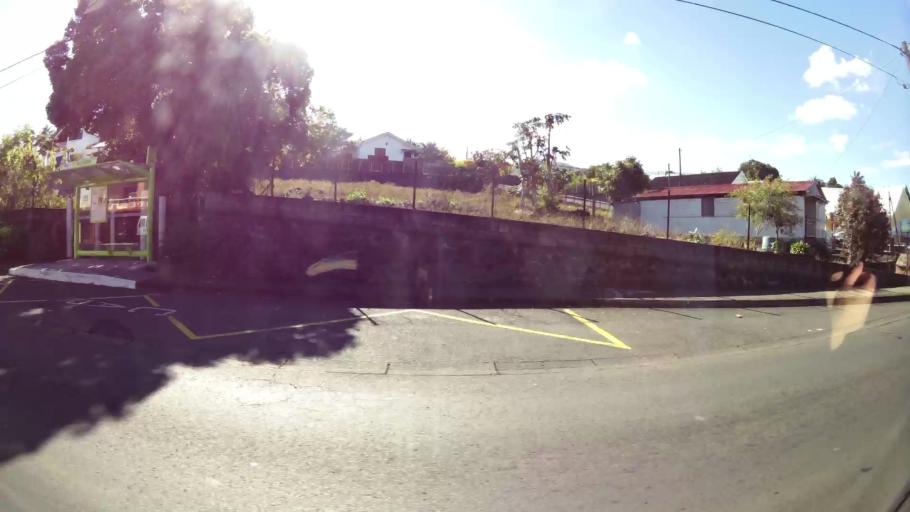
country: RE
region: Reunion
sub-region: Reunion
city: Le Tampon
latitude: -21.2706
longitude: 55.5238
